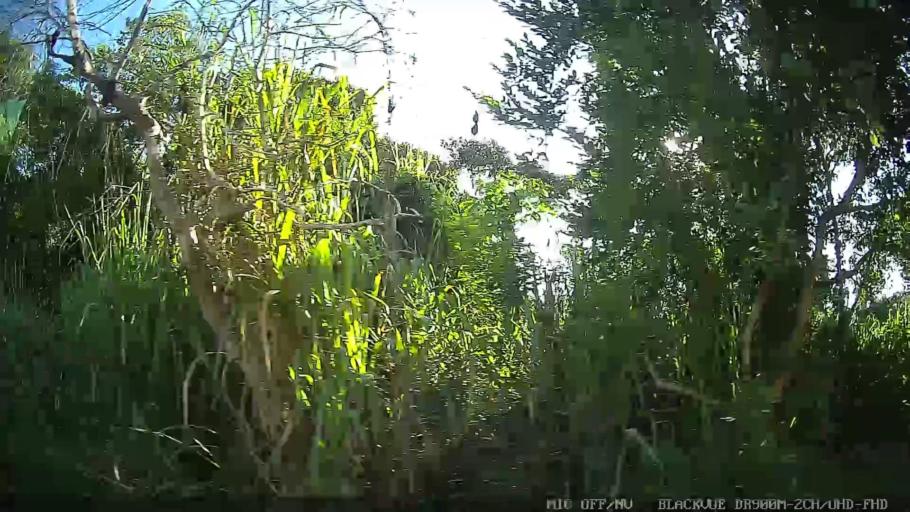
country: BR
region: Sao Paulo
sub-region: Peruibe
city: Peruibe
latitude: -24.2677
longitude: -46.9380
